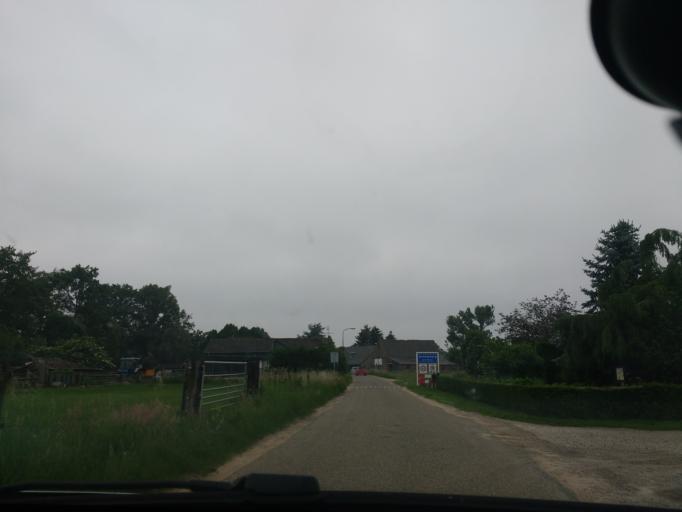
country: NL
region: Utrecht
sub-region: Gemeente Rhenen
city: Rhenen
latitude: 51.9715
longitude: 5.6010
